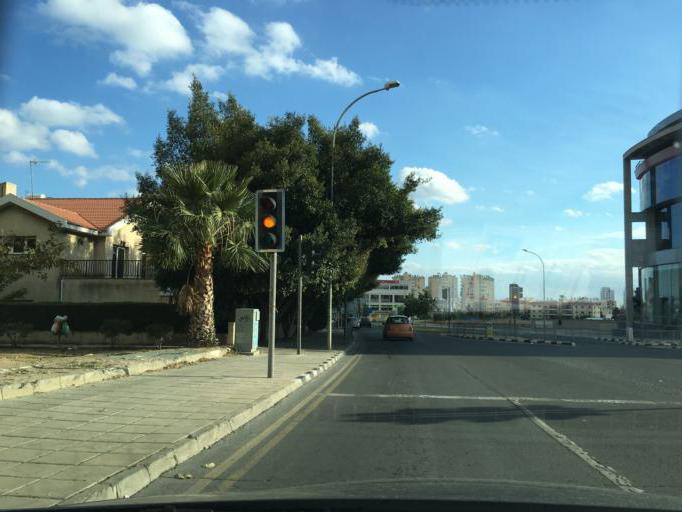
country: CY
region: Limassol
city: Limassol
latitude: 34.7005
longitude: 33.0606
